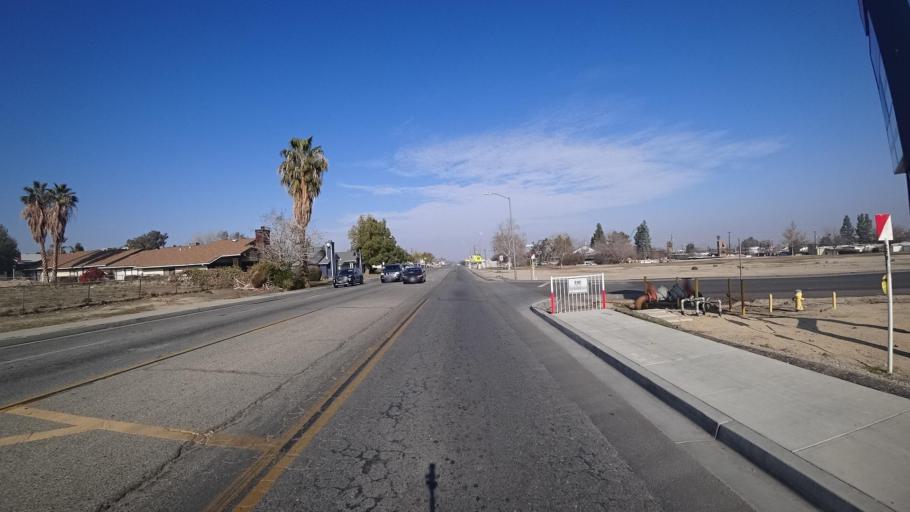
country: US
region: California
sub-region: Kern County
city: Taft
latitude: 35.1403
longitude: -119.4653
